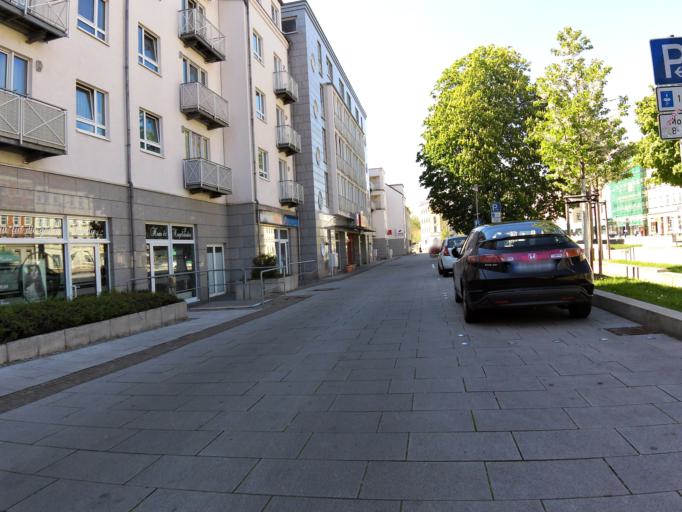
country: DE
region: Saxony
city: Leipzig
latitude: 51.3688
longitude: 12.3396
